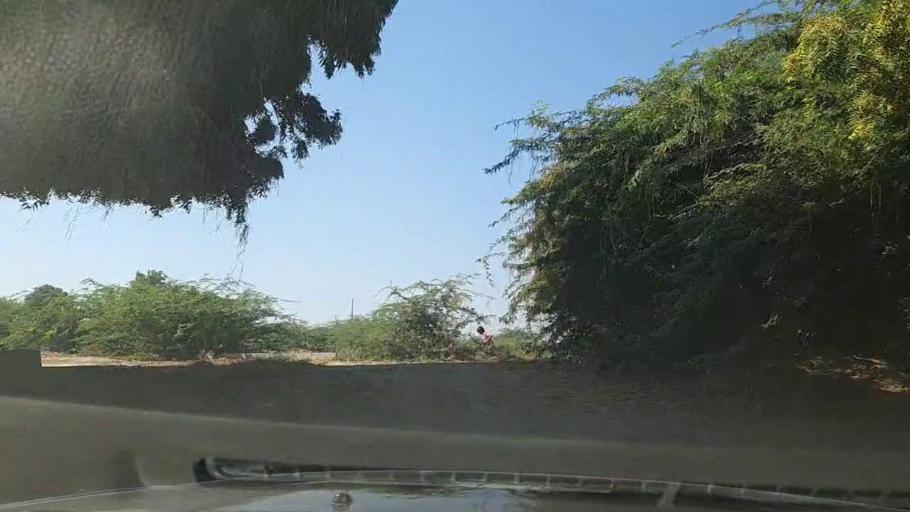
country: PK
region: Sindh
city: Mirpur Sakro
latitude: 24.5748
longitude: 67.7886
